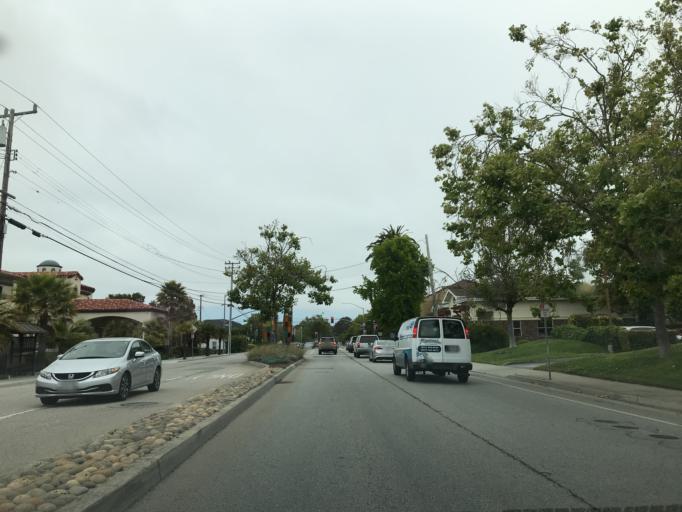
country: US
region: California
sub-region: Santa Cruz County
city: Opal Cliffs
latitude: 36.9692
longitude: -121.9648
